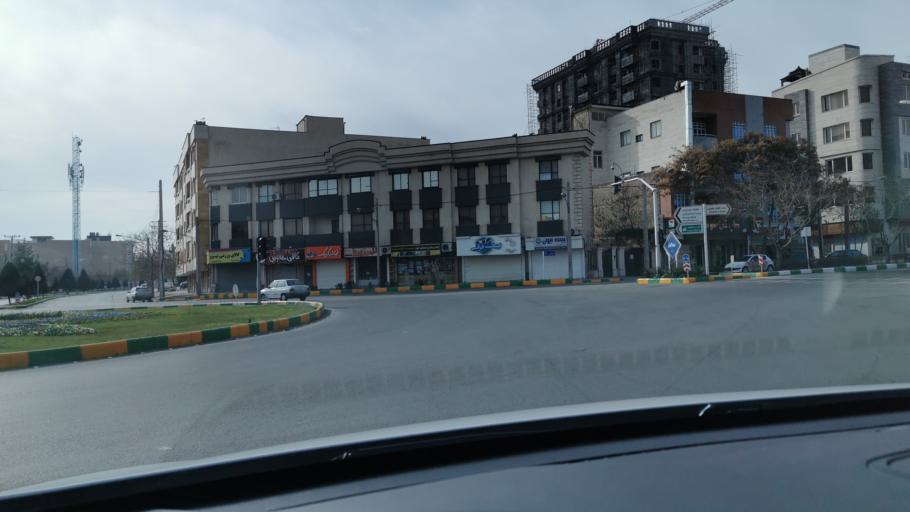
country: IR
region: Razavi Khorasan
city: Mashhad
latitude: 36.3130
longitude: 59.5148
